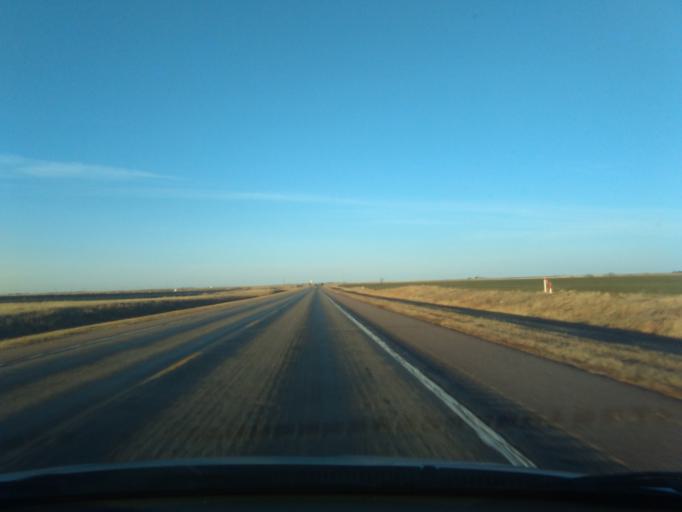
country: US
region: Nebraska
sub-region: Cheyenne County
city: Sidney
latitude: 41.2440
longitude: -102.9737
